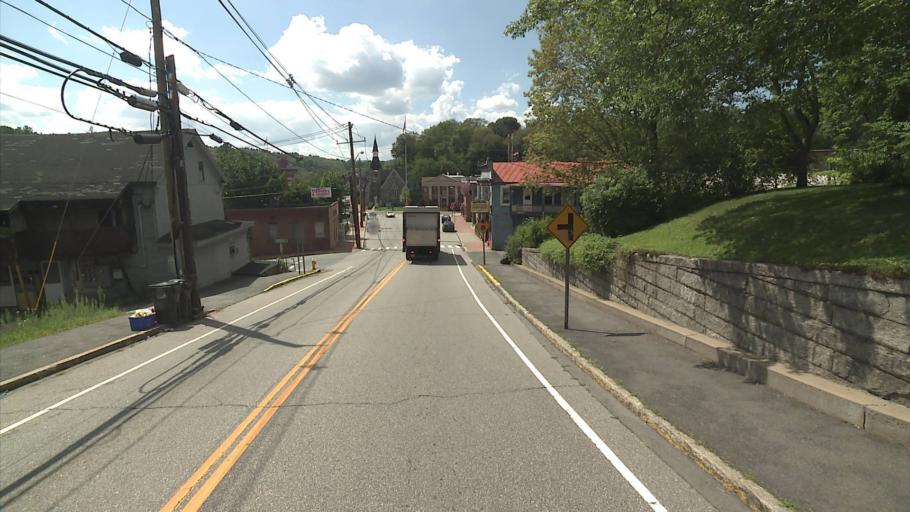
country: US
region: Connecticut
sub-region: Tolland County
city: Stafford Springs
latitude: 41.9541
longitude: -72.3015
